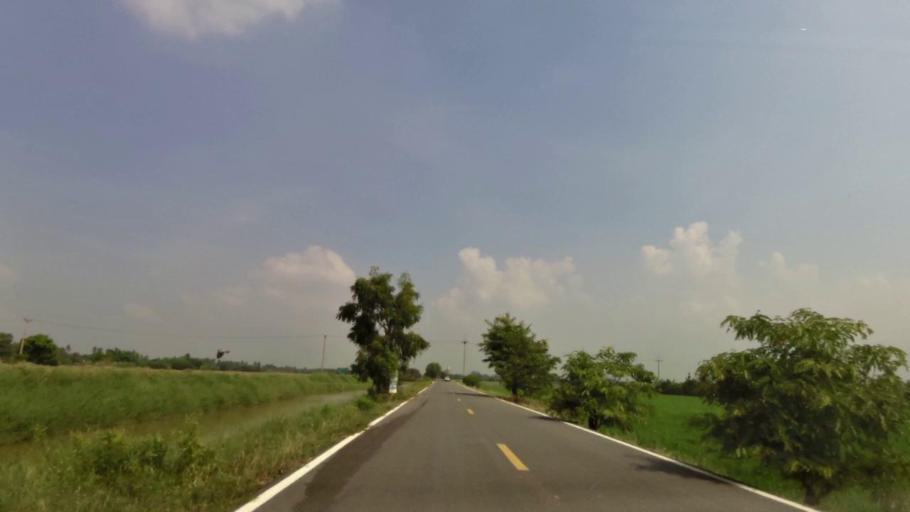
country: TH
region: Ang Thong
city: Pho Thong
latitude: 14.6183
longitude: 100.4017
